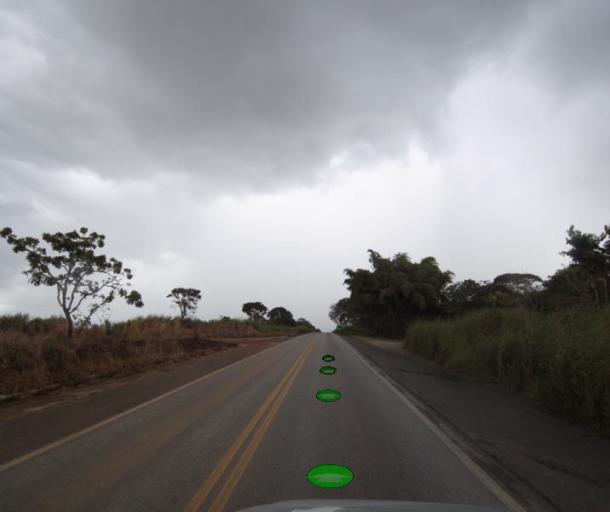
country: BR
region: Goias
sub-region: Uruacu
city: Uruacu
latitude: -14.2118
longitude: -49.1309
